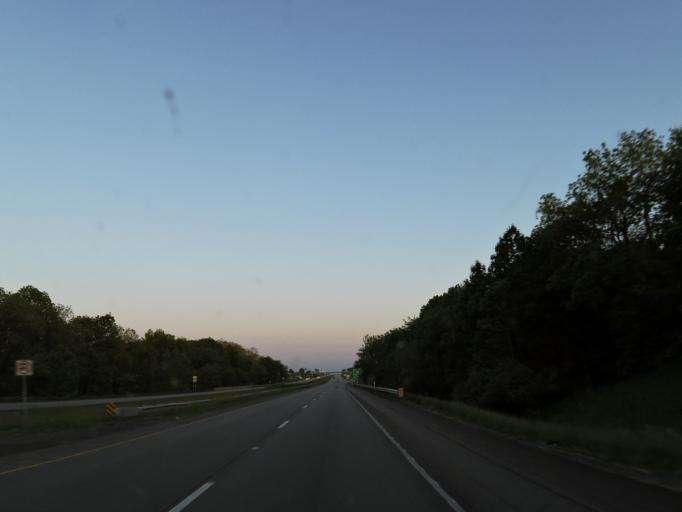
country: US
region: Indiana
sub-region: Montgomery County
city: Crawfordsville
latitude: 40.0521
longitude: -86.8186
